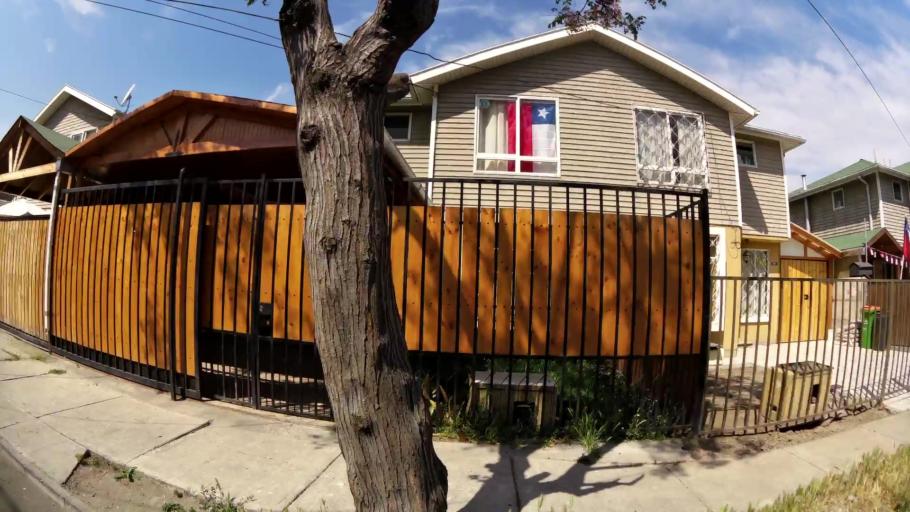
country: CL
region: Santiago Metropolitan
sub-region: Provincia de Cordillera
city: Puente Alto
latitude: -33.5801
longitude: -70.5840
